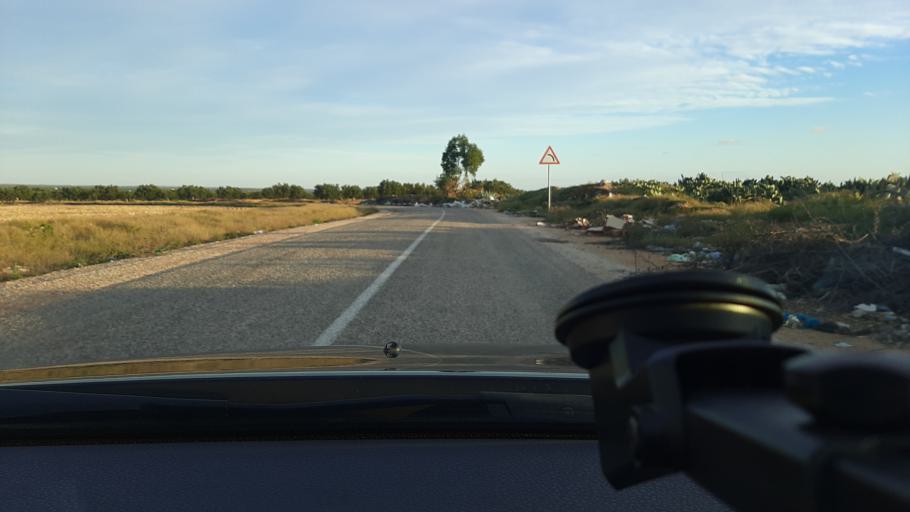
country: TN
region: Safaqis
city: Sfax
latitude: 34.9537
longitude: 10.5498
